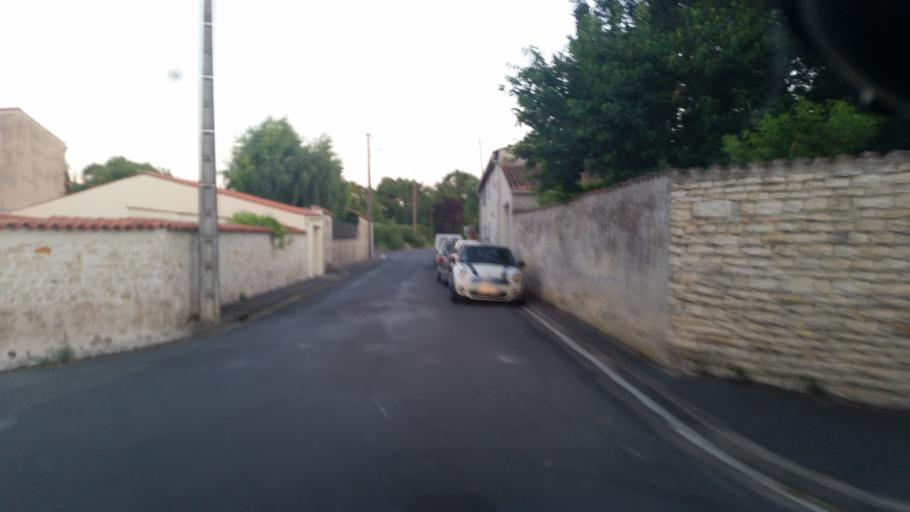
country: FR
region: Poitou-Charentes
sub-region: Departement de la Charente-Maritime
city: Marans
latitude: 46.3097
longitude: -0.9989
